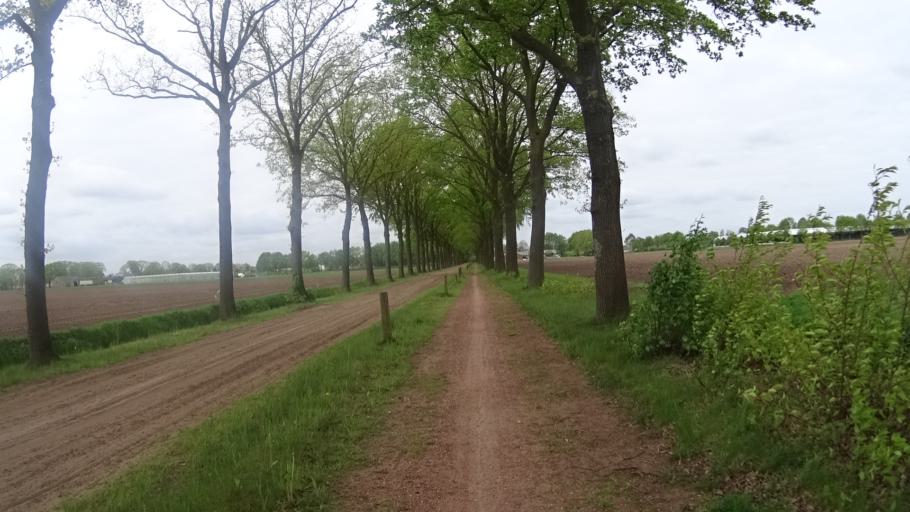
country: NL
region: North Brabant
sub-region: Gemeente Uden
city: Odiliapeel
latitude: 51.6077
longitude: 5.7219
